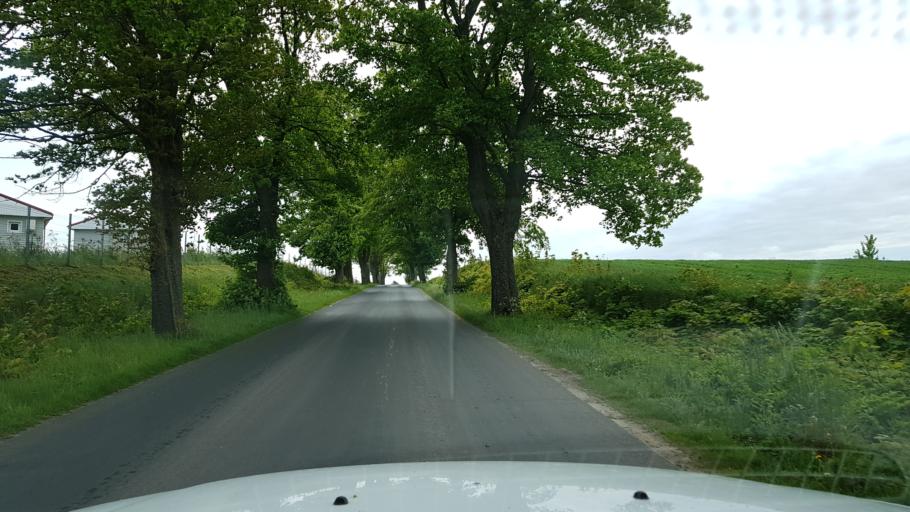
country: PL
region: West Pomeranian Voivodeship
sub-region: Powiat koszalinski
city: Mielno
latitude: 54.2420
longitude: 15.9735
